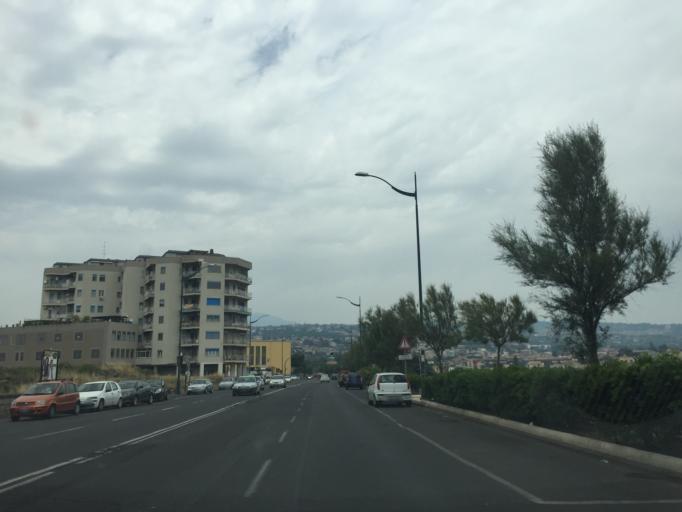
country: IT
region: Sicily
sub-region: Catania
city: Cerza
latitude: 37.5256
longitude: 15.1164
